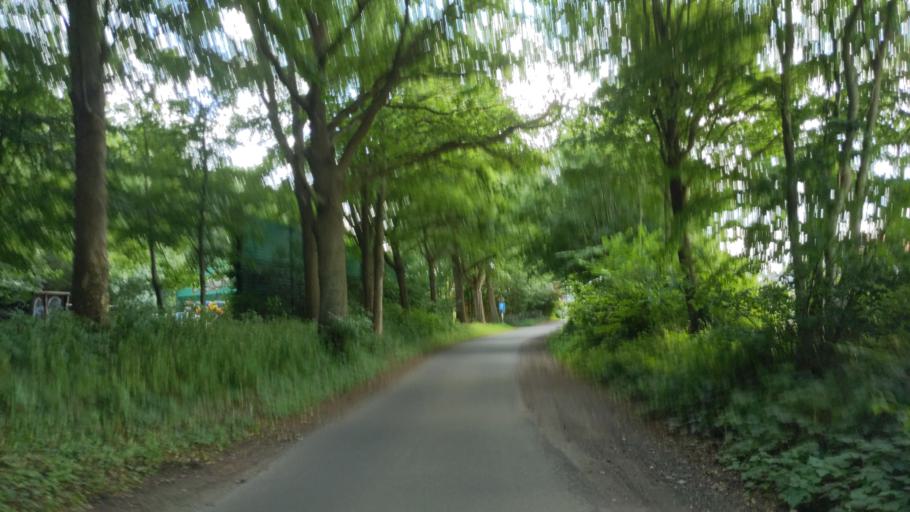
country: DE
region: Schleswig-Holstein
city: Reinfeld
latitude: 53.8375
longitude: 10.4810
